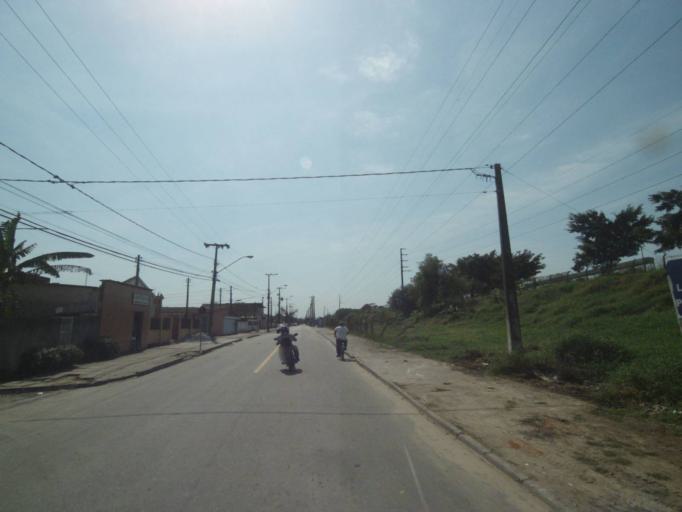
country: BR
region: Parana
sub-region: Paranagua
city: Paranagua
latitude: -25.5437
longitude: -48.5482
